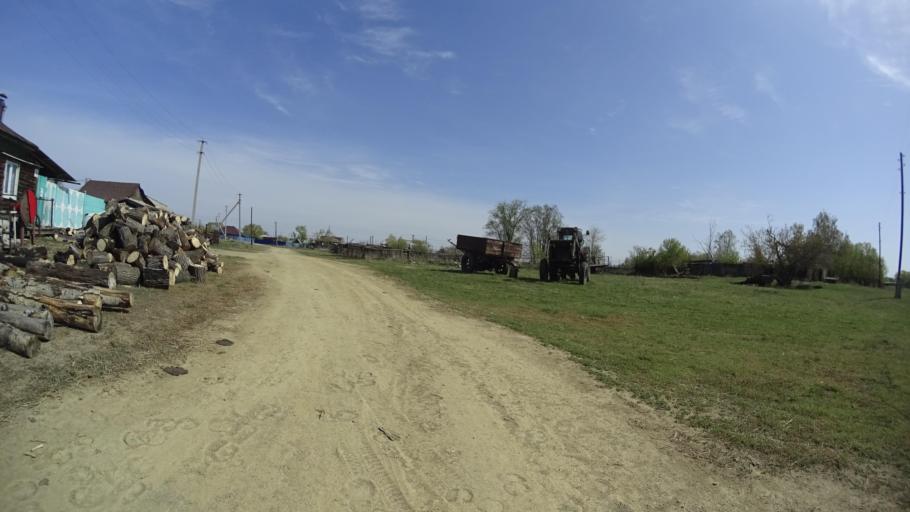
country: RU
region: Chelyabinsk
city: Chesma
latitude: 53.7983
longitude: 61.0173
